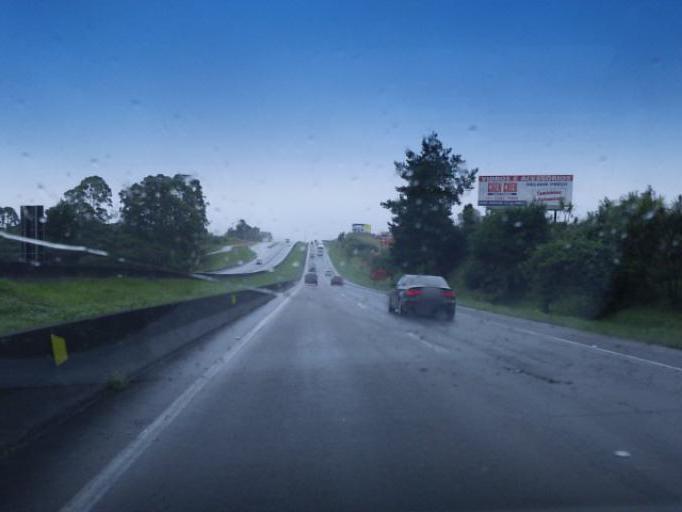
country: BR
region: Parana
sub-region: Sao Jose Dos Pinhais
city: Sao Jose dos Pinhais
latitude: -25.6271
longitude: -49.1649
